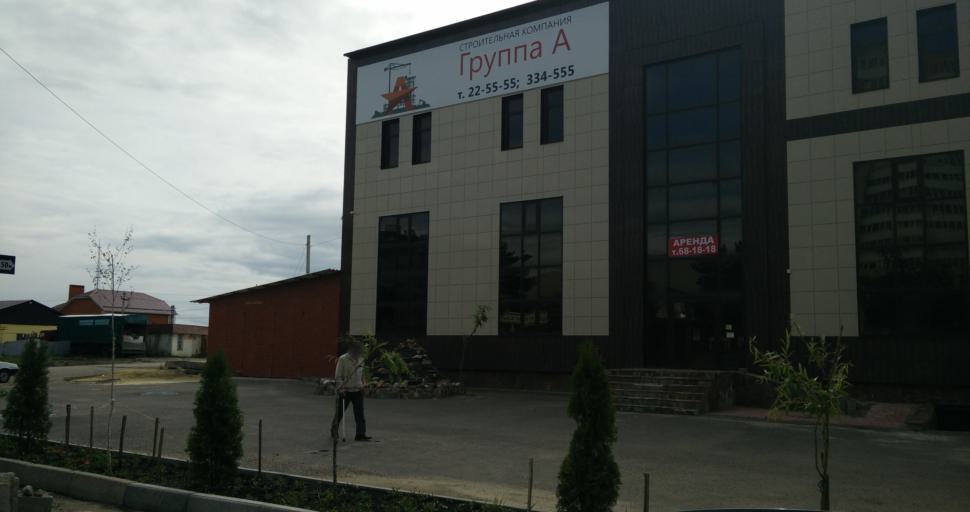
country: RU
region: Stavropol'skiy
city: Tatarka
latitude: 44.9851
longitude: 41.9208
